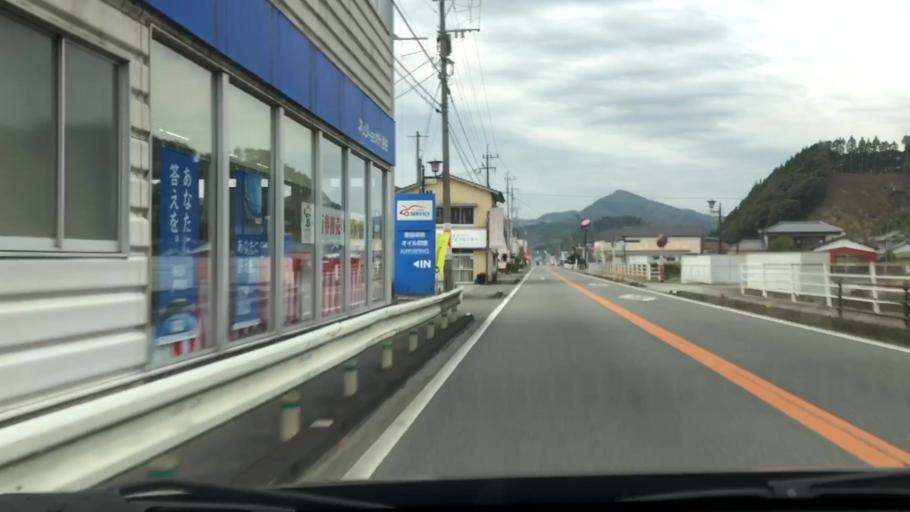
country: JP
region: Oita
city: Saiki
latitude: 32.9768
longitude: 131.8452
